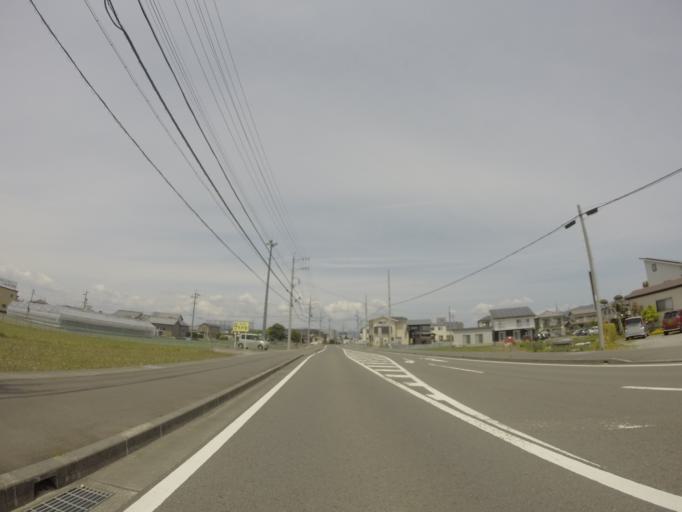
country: JP
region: Shizuoka
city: Fujieda
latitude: 34.8430
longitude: 138.2929
